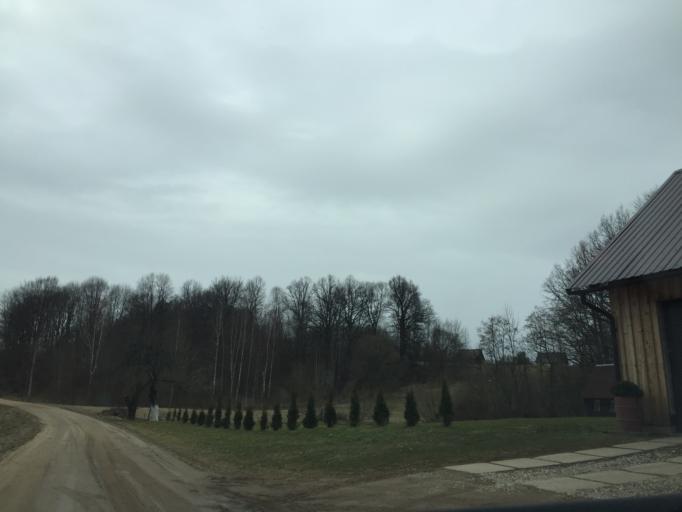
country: LV
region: Kraslavas Rajons
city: Kraslava
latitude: 55.9783
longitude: 27.1679
